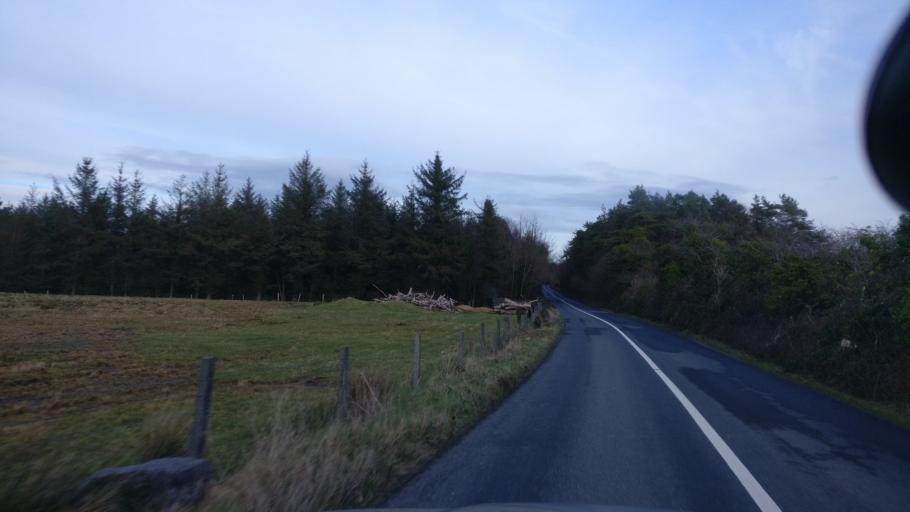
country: IE
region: Connaught
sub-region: County Galway
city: Oughterard
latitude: 53.5312
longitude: -9.3332
